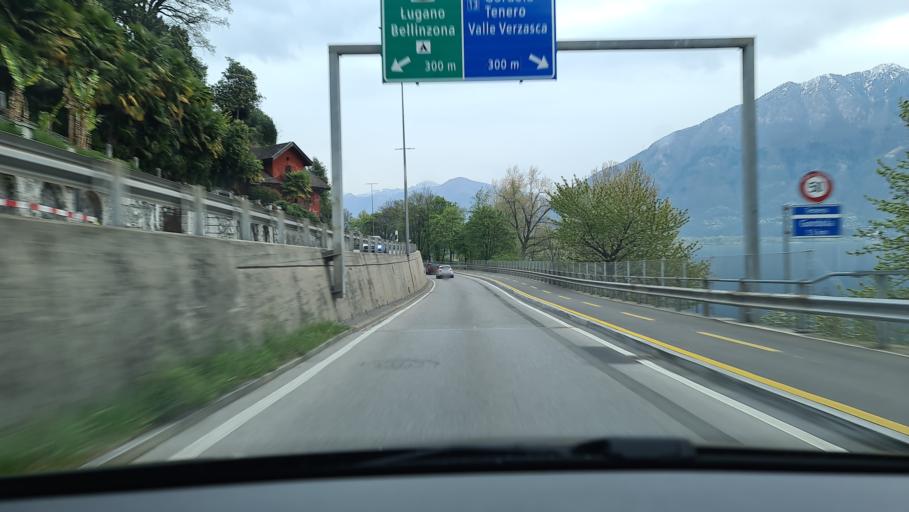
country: CH
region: Ticino
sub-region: Locarno District
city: Minusio
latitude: 46.1801
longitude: 8.8349
